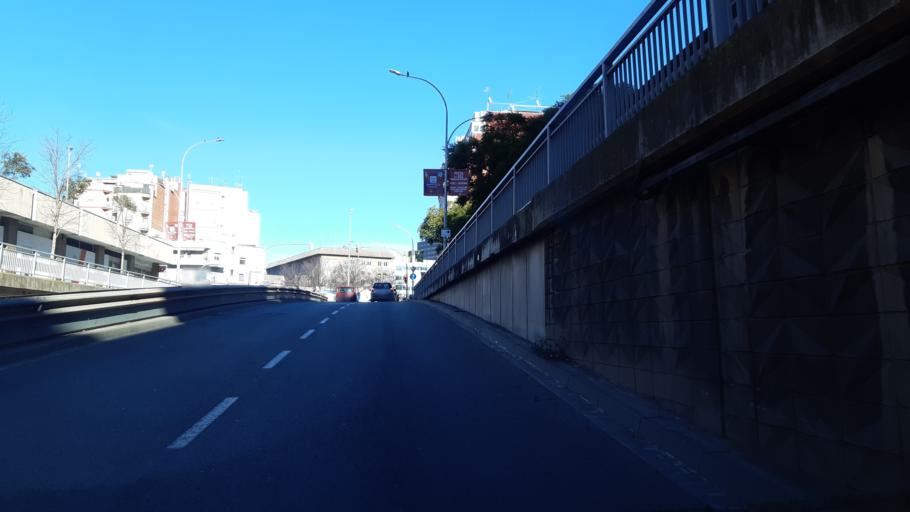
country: ES
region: Catalonia
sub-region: Provincia de Barcelona
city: L'Hospitalet de Llobregat
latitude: 41.3722
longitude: 2.1054
